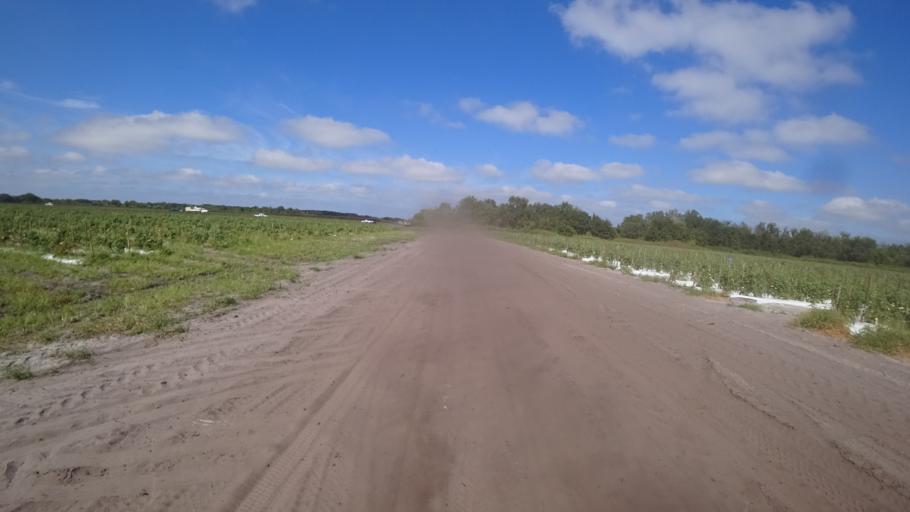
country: US
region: Florida
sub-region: DeSoto County
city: Arcadia
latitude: 27.2841
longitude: -82.0784
